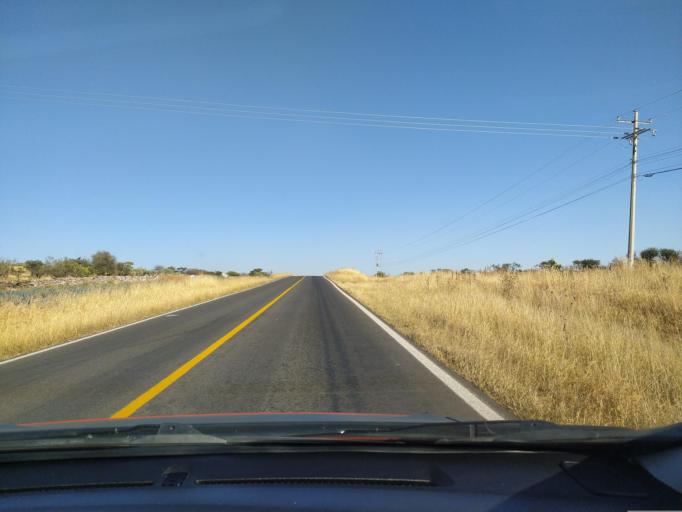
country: MX
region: Jalisco
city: San Miguel el Alto
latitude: 21.0235
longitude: -102.4369
